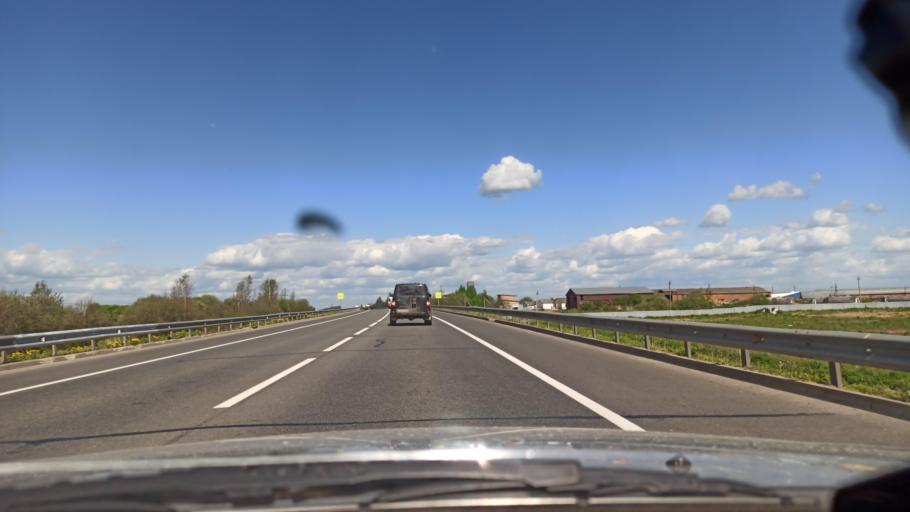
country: RU
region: Vologda
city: Vologda
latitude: 59.2795
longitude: 39.8333
